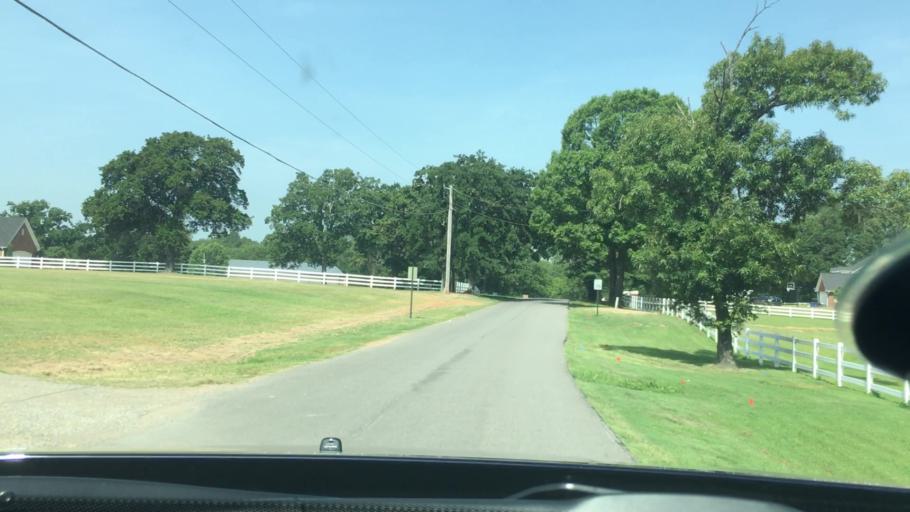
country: US
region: Oklahoma
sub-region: Atoka County
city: Atoka
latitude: 34.3603
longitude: -96.1543
